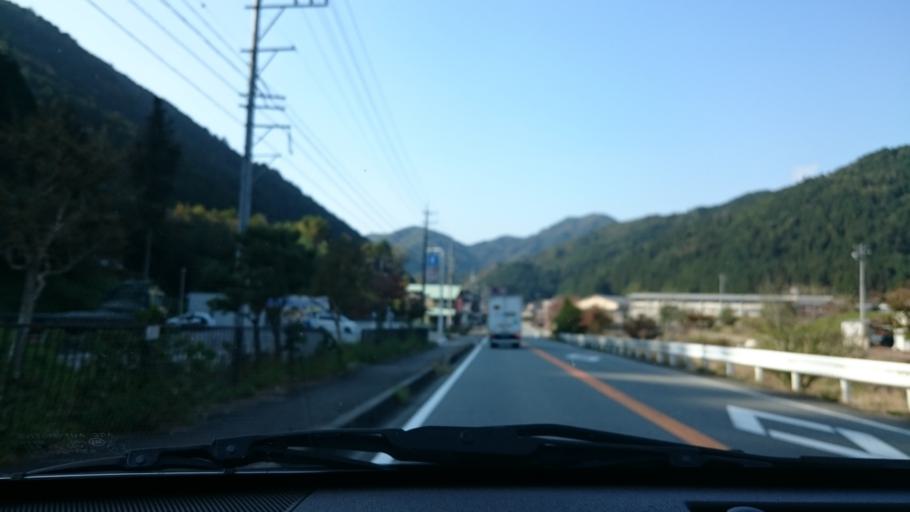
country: JP
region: Gifu
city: Gujo
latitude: 35.7651
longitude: 137.2883
